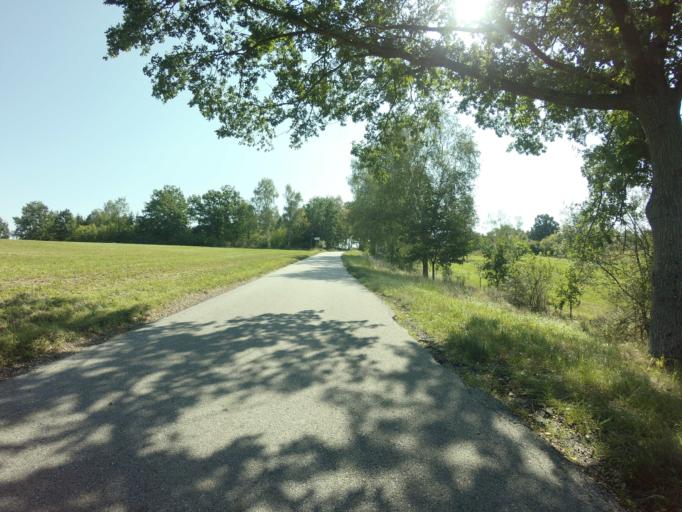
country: CZ
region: Jihocesky
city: Kamenny Ujezd
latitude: 48.8902
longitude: 14.4195
